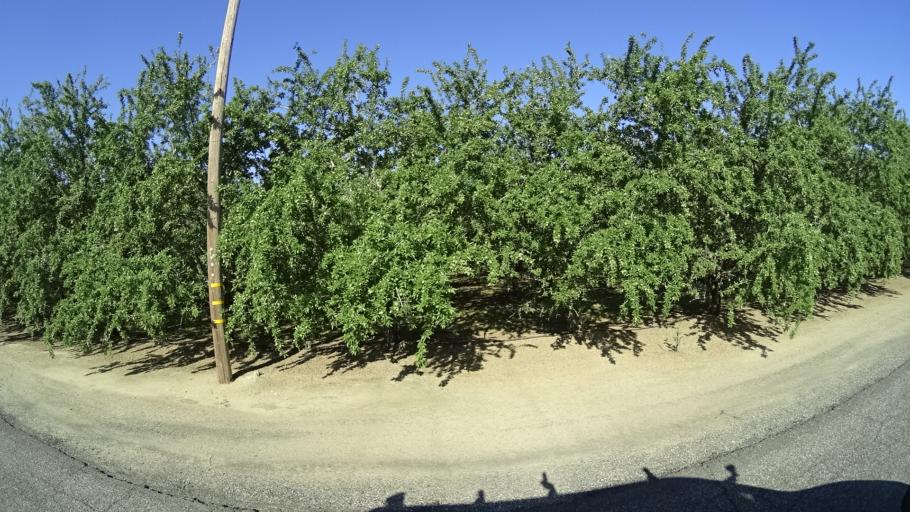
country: US
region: California
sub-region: Glenn County
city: Hamilton City
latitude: 39.6987
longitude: -122.0548
